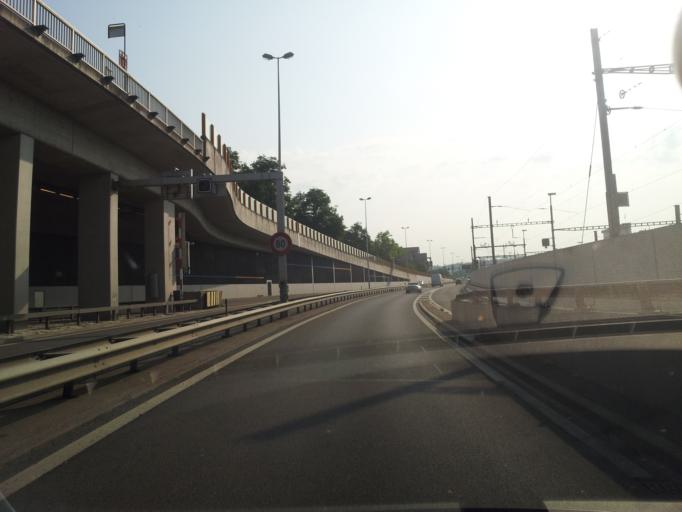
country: CH
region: Schaffhausen
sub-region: Bezirk Schaffhausen
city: Schaffhausen
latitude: 47.7107
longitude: 8.6418
